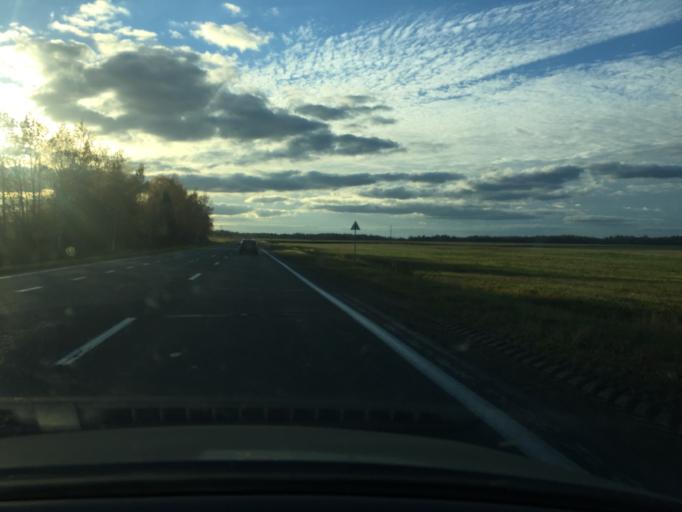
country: BY
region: Vitebsk
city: Vyerkhnyadzvinsk
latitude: 55.8368
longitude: 27.8372
